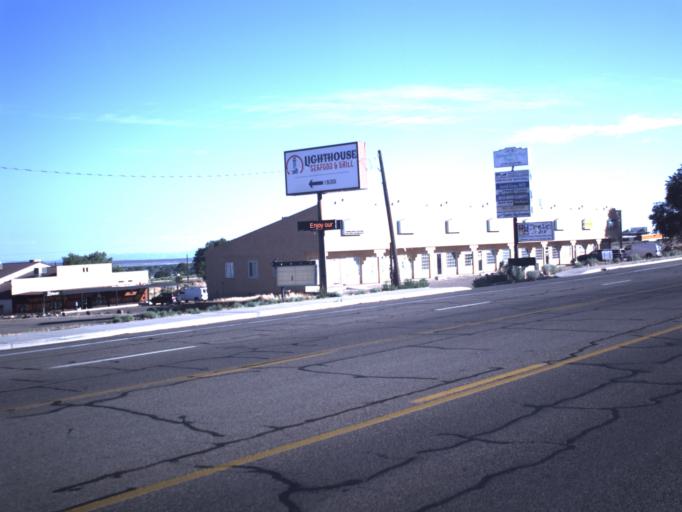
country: US
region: Utah
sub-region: Iron County
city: Cedar City
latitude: 37.7150
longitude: -113.0601
